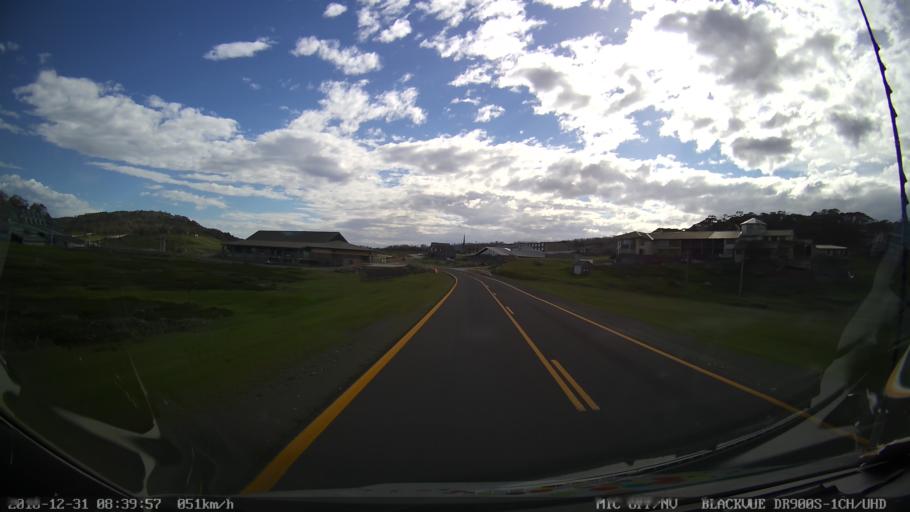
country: AU
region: New South Wales
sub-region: Snowy River
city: Jindabyne
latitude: -36.4064
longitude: 148.4103
